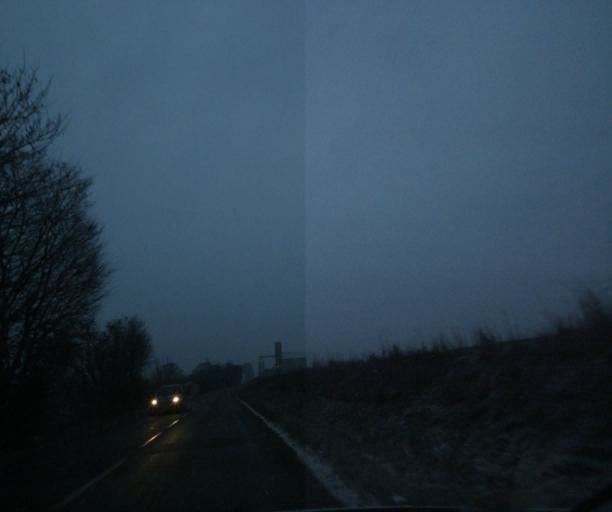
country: FR
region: Champagne-Ardenne
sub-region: Departement de la Haute-Marne
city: Wassy
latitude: 48.4306
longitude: 4.9624
